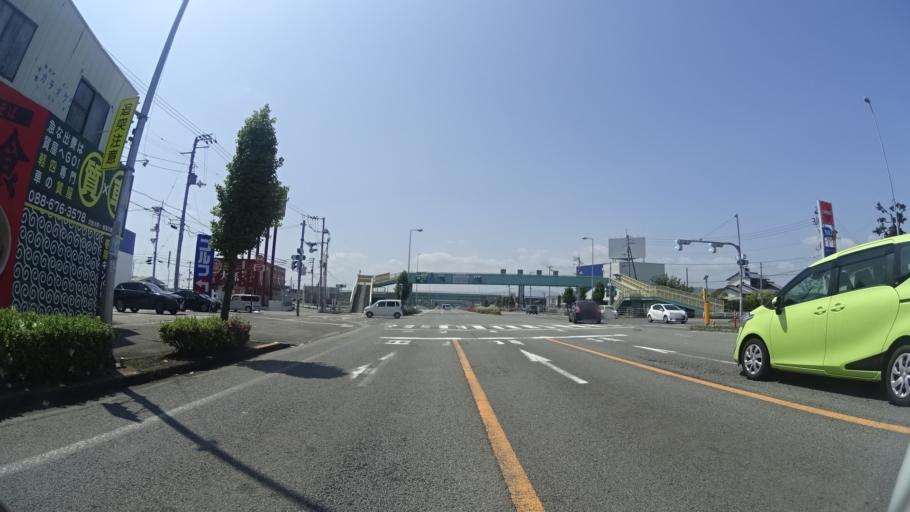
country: JP
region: Tokushima
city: Tokushima-shi
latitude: 34.1060
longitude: 134.5763
